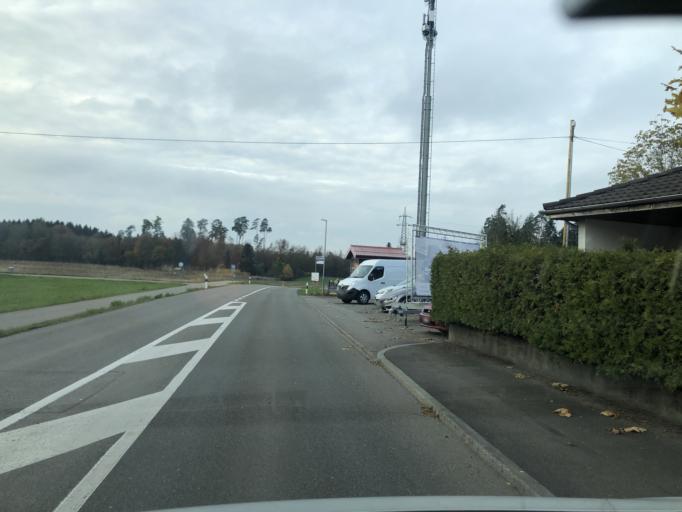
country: CH
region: Aargau
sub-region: Bezirk Baden
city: Mellingen
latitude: 47.4435
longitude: 8.2810
